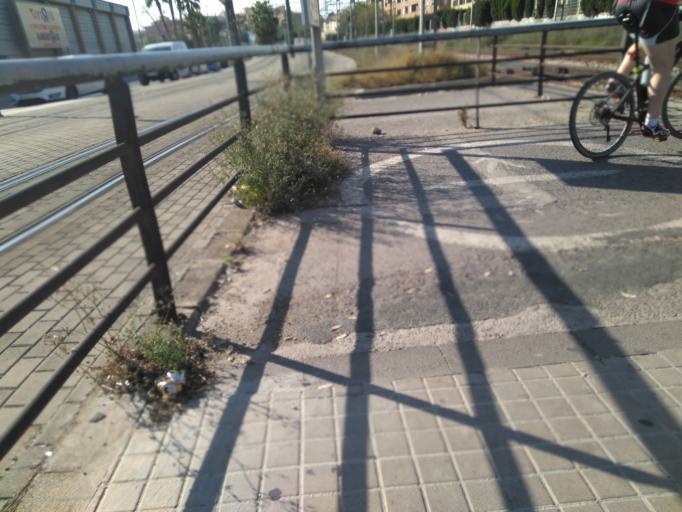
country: ES
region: Valencia
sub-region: Provincia de Valencia
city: Burjassot
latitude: 39.5009
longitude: -0.4038
